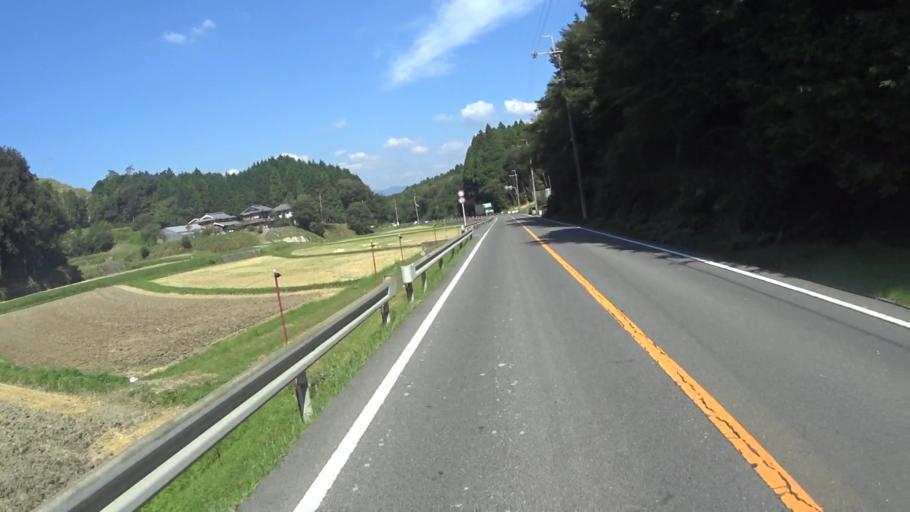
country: JP
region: Kyoto
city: Kameoka
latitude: 34.9748
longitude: 135.5207
